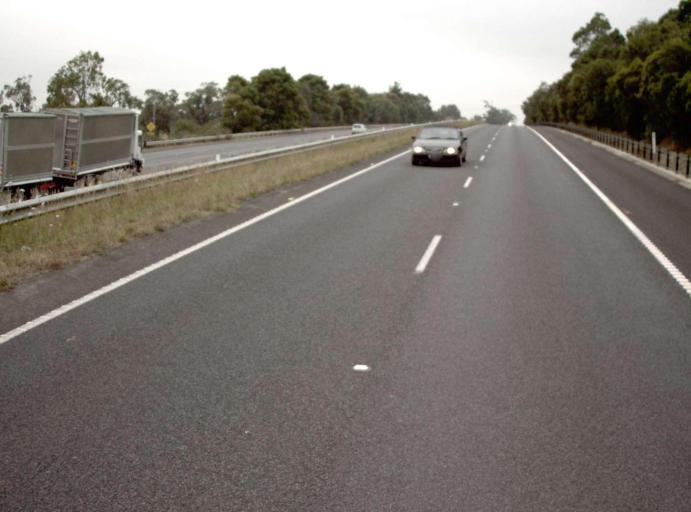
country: AU
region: Victoria
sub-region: Latrobe
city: Moe
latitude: -38.1988
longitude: 146.1968
